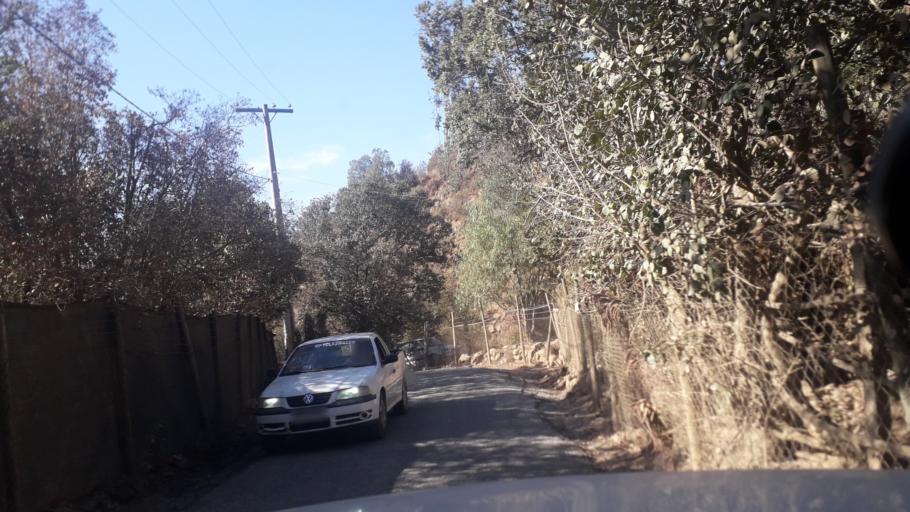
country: CL
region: Valparaiso
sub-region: Provincia de Marga Marga
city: Limache
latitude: -33.0765
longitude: -71.0992
